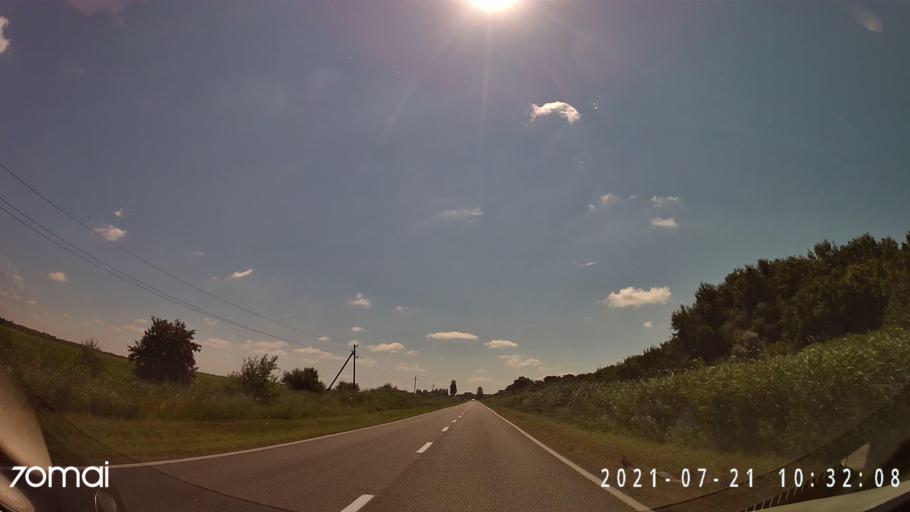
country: RO
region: Tulcea
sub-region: Oras Isaccea
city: Isaccea
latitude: 45.3037
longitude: 28.4166
